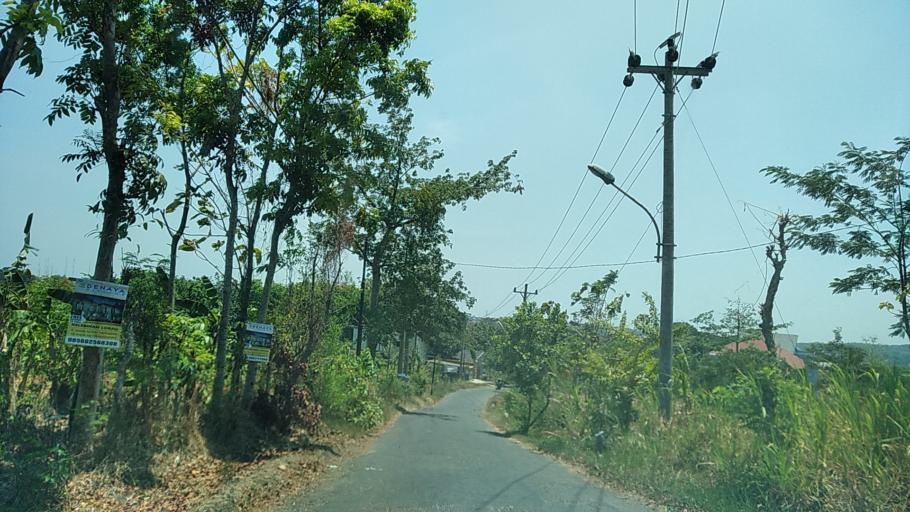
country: ID
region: Central Java
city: Ungaran
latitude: -7.0843
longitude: 110.4263
